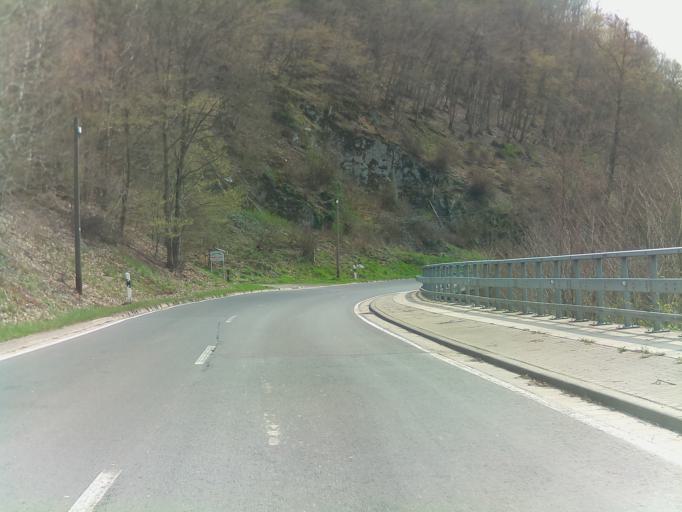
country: DE
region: Rheinland-Pfalz
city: Bruschied
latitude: 49.8296
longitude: 7.3970
